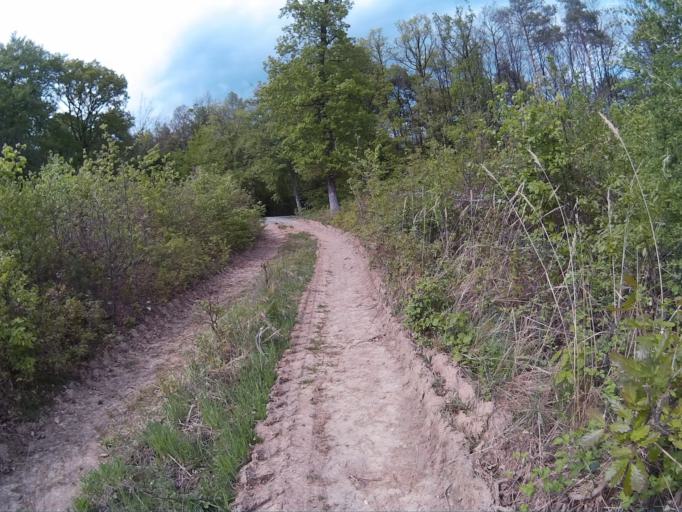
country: HU
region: Vas
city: Koszeg
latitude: 47.3673
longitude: 16.5012
